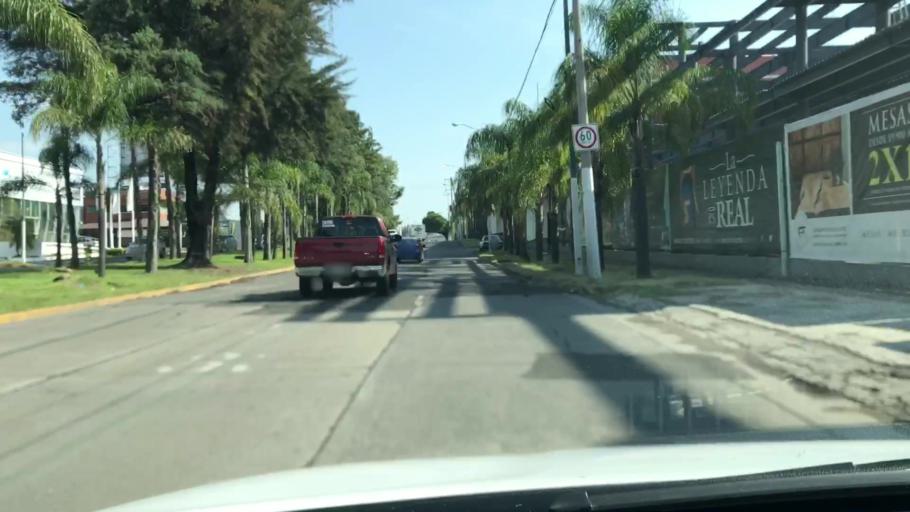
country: MX
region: Jalisco
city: Guadalajara
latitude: 20.6744
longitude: -103.4223
